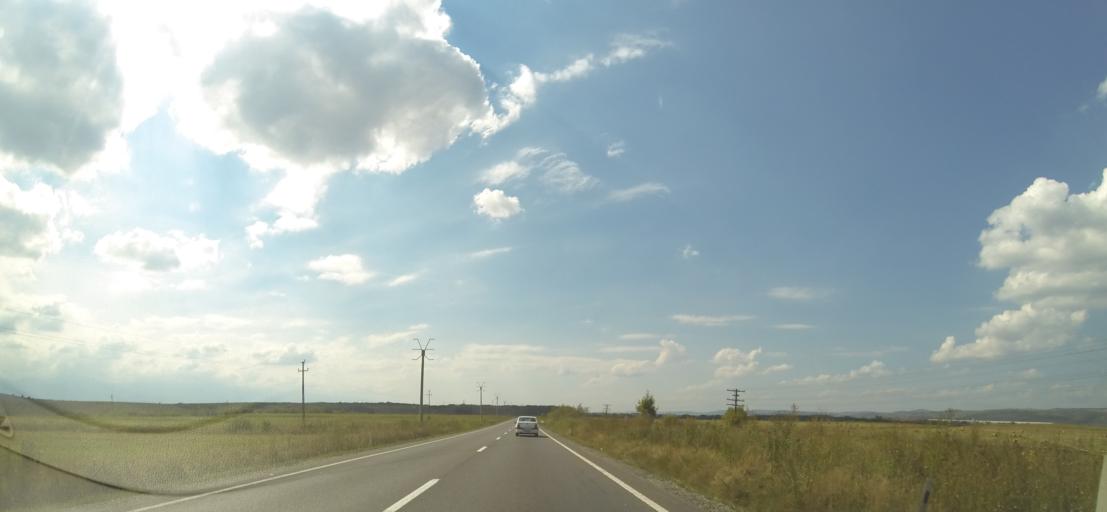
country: RO
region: Brasov
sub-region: Comuna Mandra
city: Mandra
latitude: 45.8232
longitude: 25.0820
